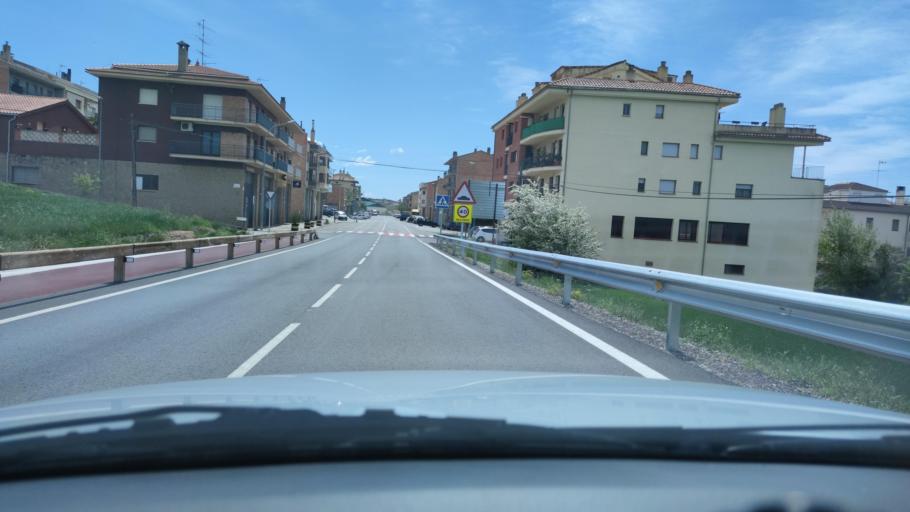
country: ES
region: Catalonia
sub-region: Provincia de Lleida
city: Solsona
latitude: 42.0013
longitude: 1.5177
